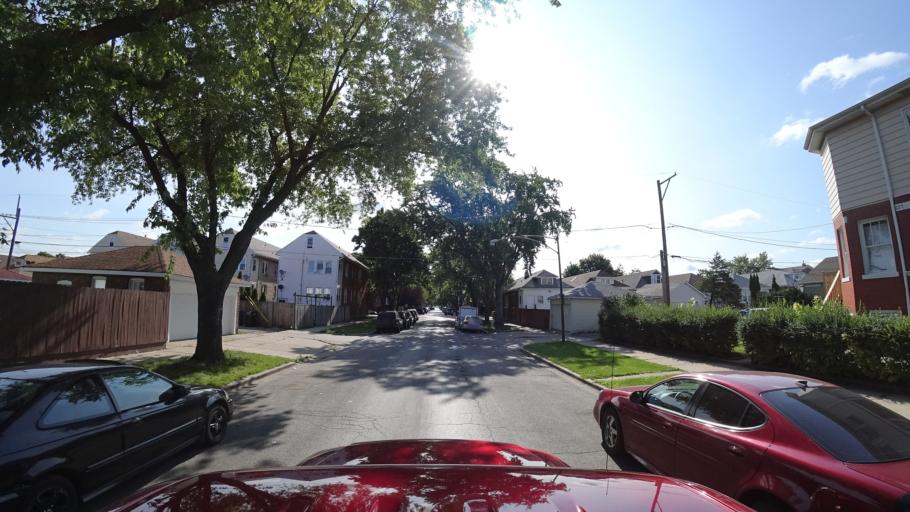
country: US
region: Illinois
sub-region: Cook County
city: Hometown
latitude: 41.7881
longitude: -87.7007
